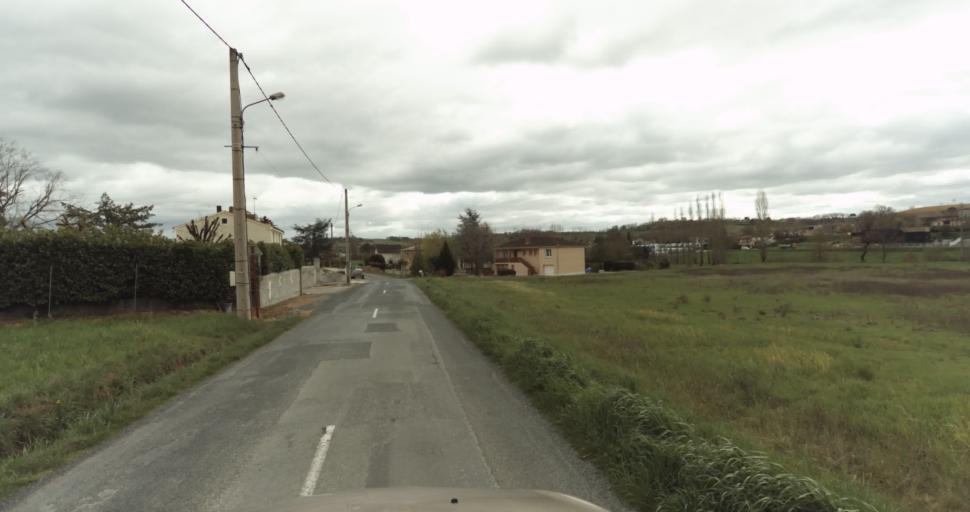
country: FR
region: Midi-Pyrenees
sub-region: Departement du Tarn
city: Puygouzon
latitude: 43.8984
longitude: 2.1542
